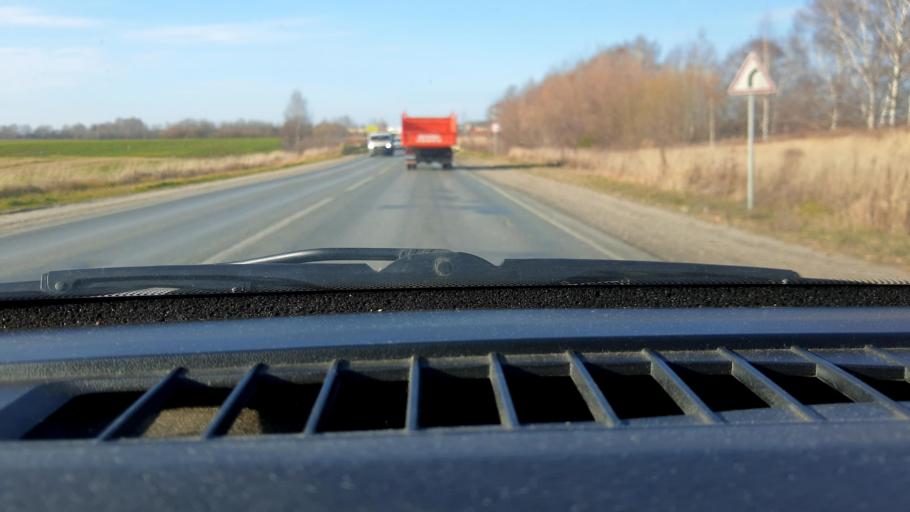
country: RU
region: Nizjnij Novgorod
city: Gorodets
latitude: 56.6386
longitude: 43.5126
